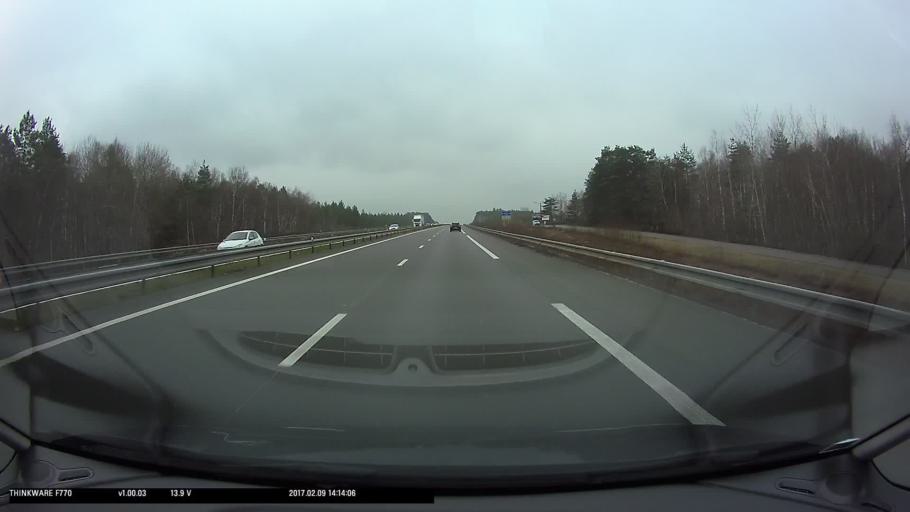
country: FR
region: Centre
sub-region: Departement du Loir-et-Cher
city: Theillay
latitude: 47.3660
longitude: 2.0534
